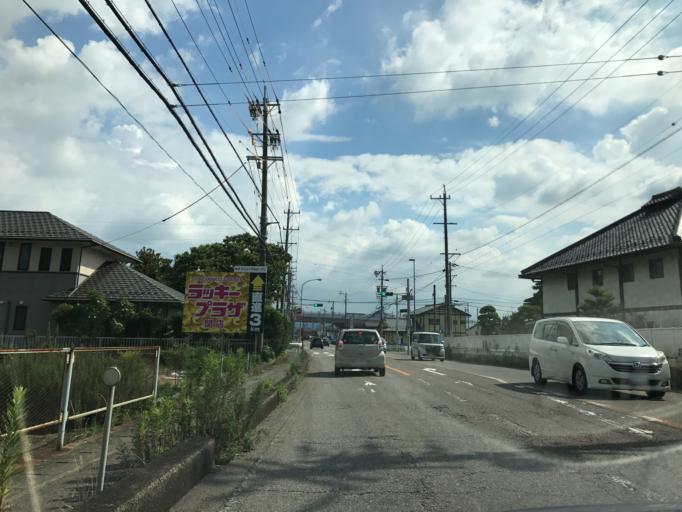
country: JP
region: Gifu
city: Mino
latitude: 35.5226
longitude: 136.9070
